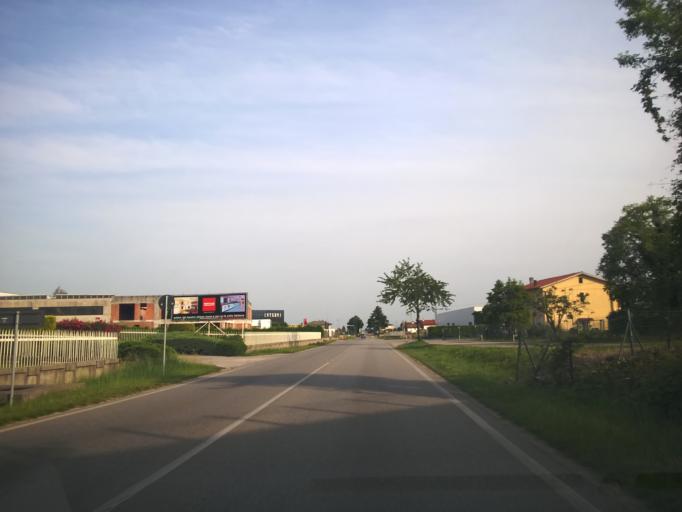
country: IT
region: Veneto
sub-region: Provincia di Vicenza
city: Piovene Rocchette
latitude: 45.7414
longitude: 11.4377
